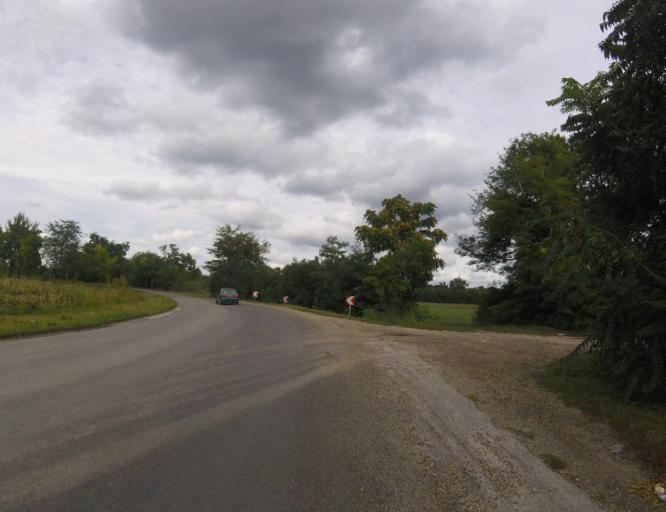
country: HU
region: Pest
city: Szigetcsep
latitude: 47.2852
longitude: 18.9834
